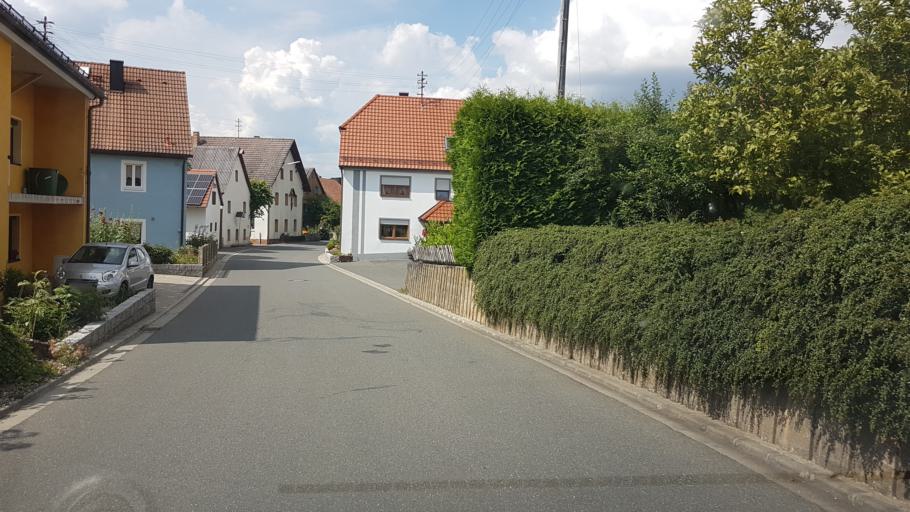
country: DE
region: Bavaria
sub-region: Upper Franconia
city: Egloffstein
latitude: 49.7536
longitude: 11.2662
